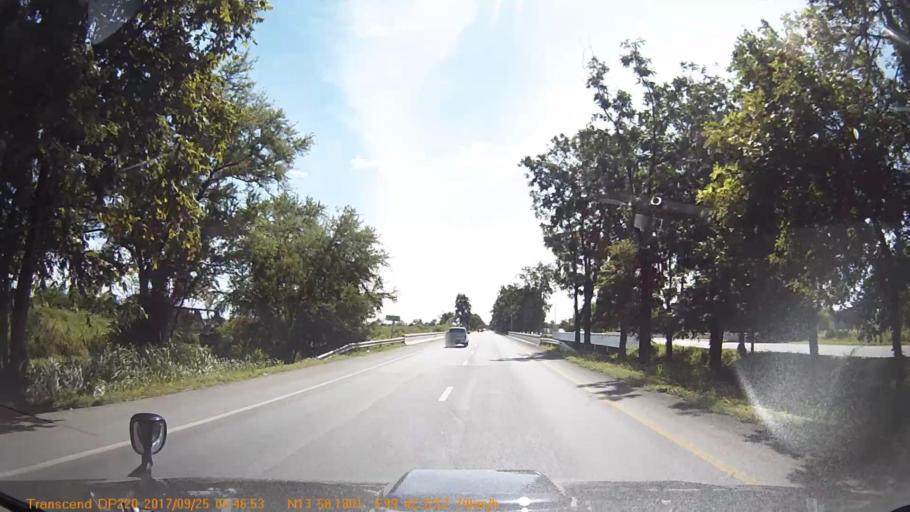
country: TH
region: Kanchanaburi
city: Tha Muang
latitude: 13.9696
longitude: 99.7059
